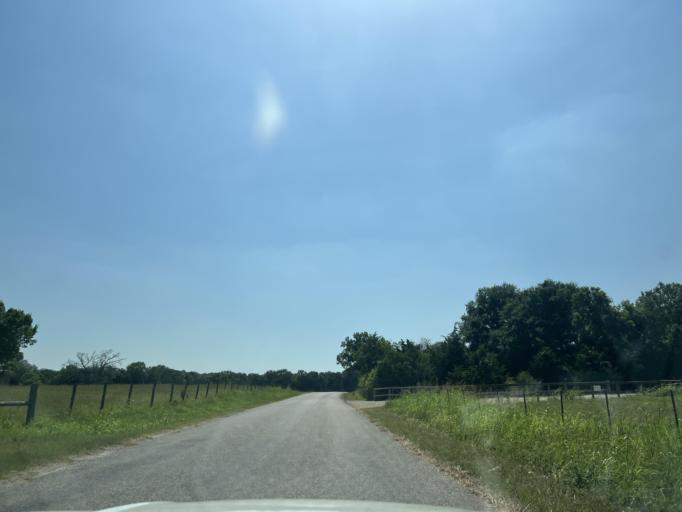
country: US
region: Texas
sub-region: Washington County
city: Brenham
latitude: 30.1535
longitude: -96.4744
